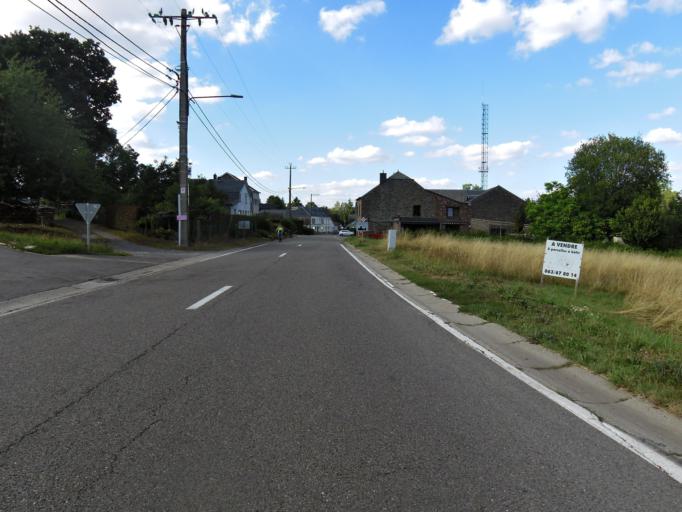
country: BE
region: Wallonia
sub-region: Province de Namur
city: Bievre
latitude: 49.9313
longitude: 5.0424
